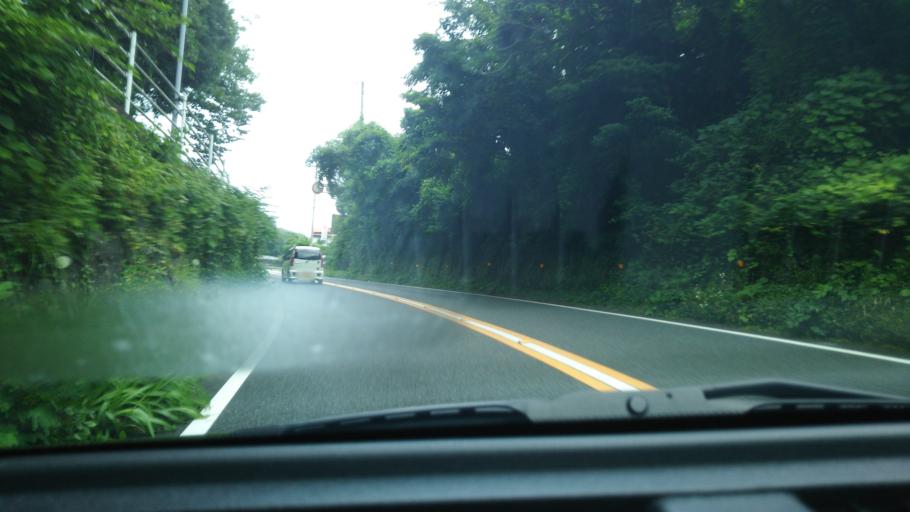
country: JP
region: Shizuoka
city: Ito
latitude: 34.8591
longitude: 139.0887
